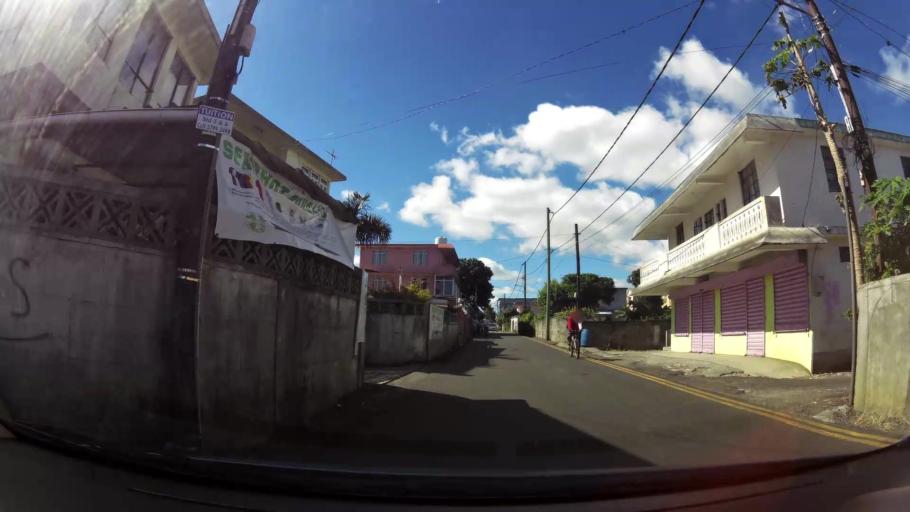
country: MU
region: Plaines Wilhems
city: Vacoas
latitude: -20.2914
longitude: 57.4807
